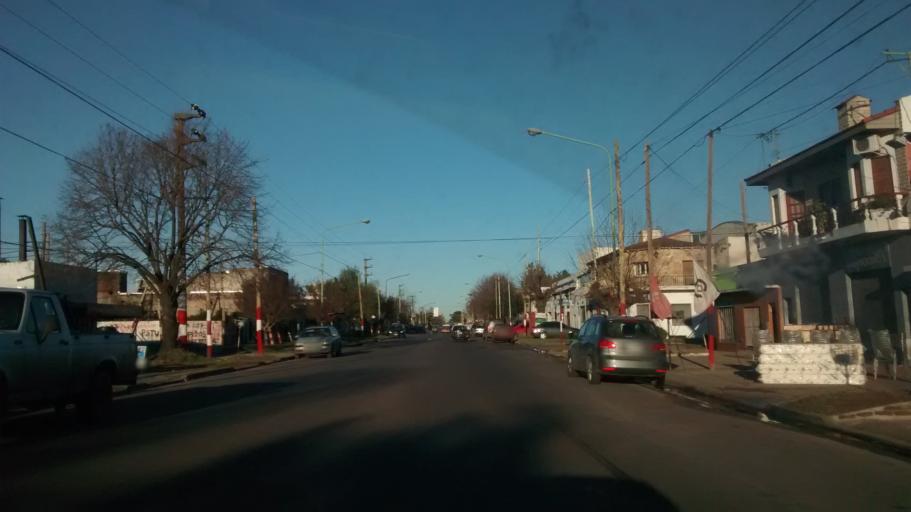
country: AR
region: Buenos Aires
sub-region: Partido de La Plata
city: La Plata
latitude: -34.9577
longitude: -57.9695
